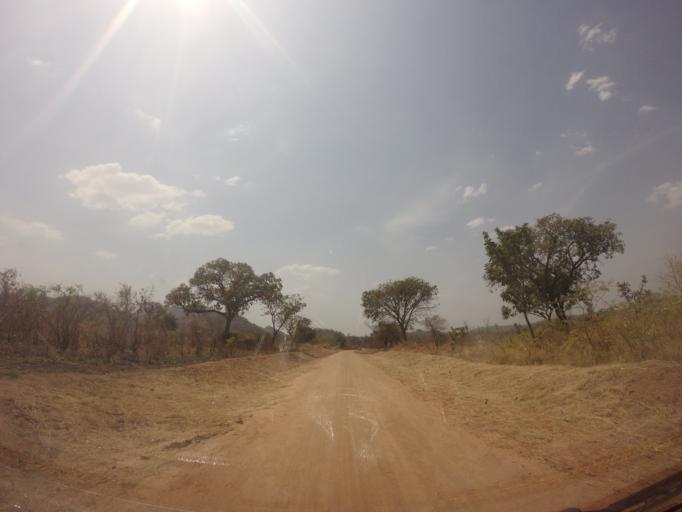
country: UG
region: Northern Region
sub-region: Arua District
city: Arua
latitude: 2.8969
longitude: 31.1144
